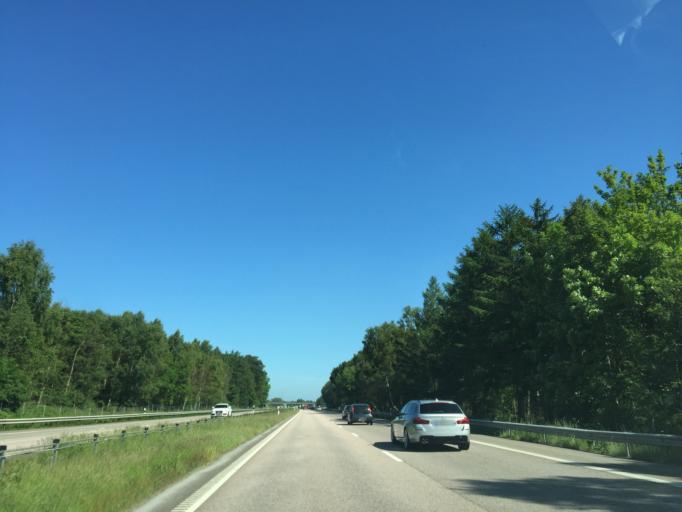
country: SE
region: Skane
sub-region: Helsingborg
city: Odakra
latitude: 56.0583
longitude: 12.7831
